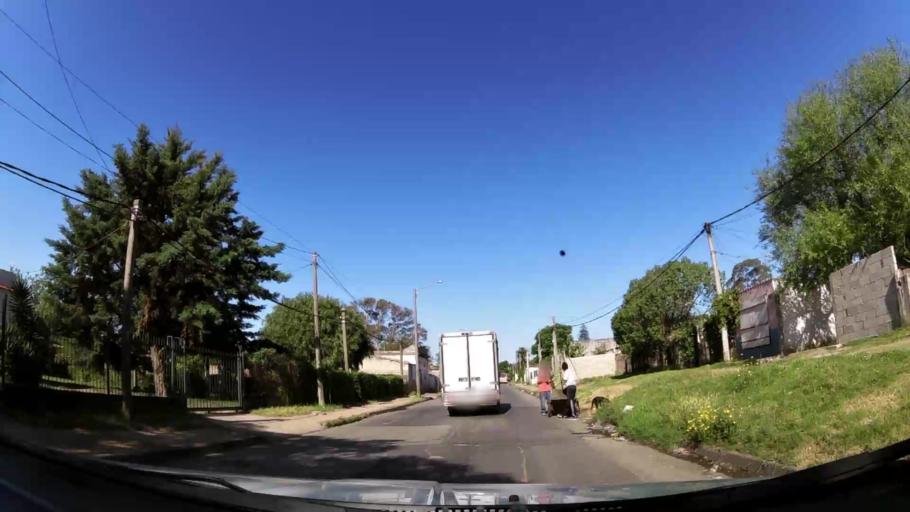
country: UY
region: Montevideo
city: Montevideo
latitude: -34.8341
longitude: -56.1538
